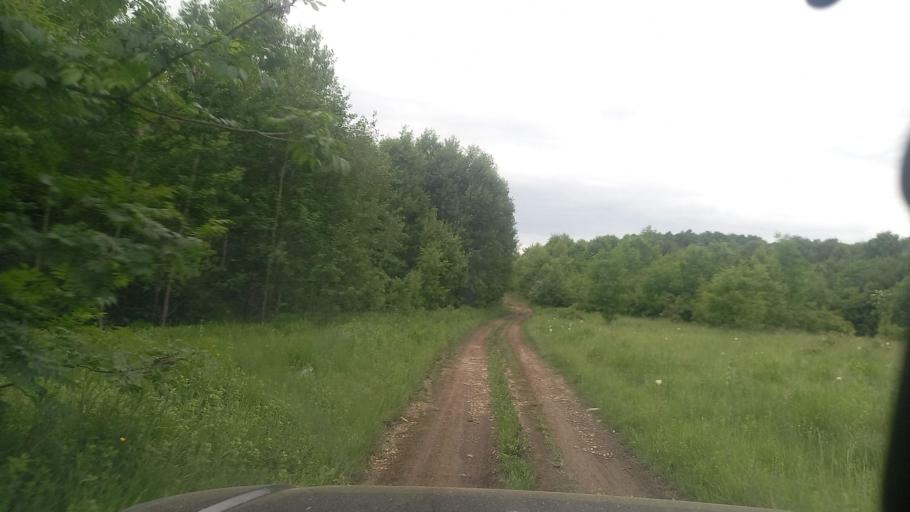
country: RU
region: Karachayevo-Cherkesiya
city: Pregradnaya
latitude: 44.0370
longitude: 41.3202
